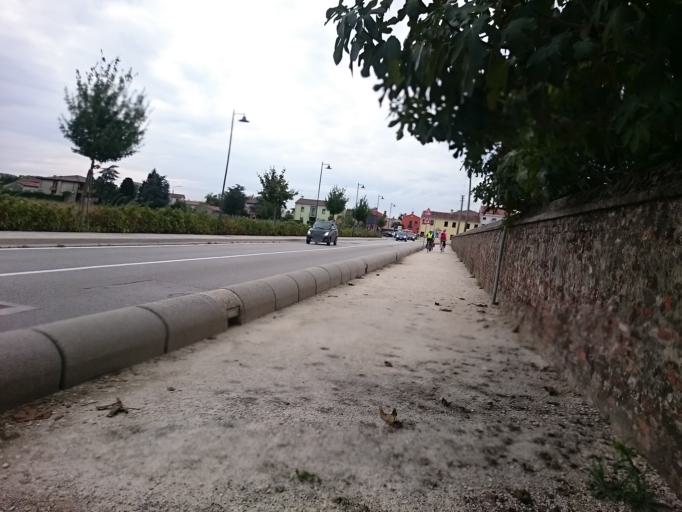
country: IT
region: Veneto
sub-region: Provincia di Vicenza
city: Grumolo delle Abbadesse
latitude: 45.4984
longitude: 11.6686
